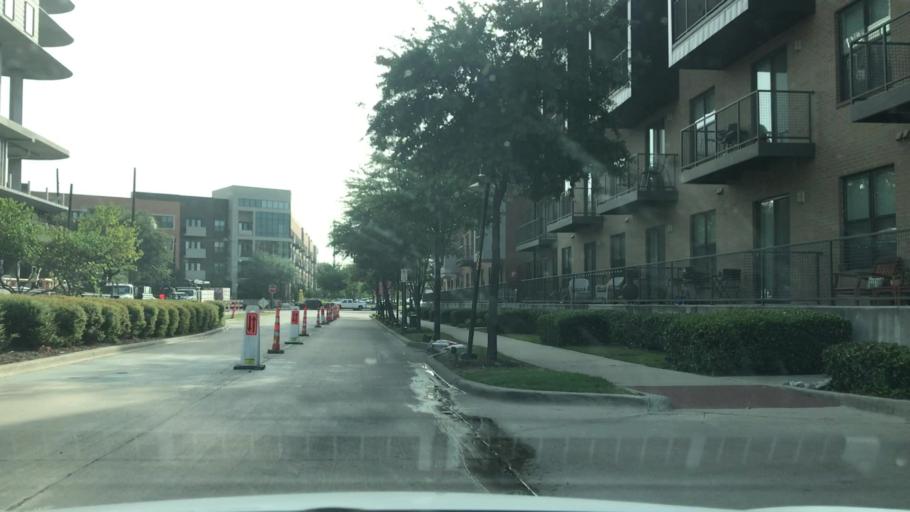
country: US
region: Texas
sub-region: Dallas County
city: Dallas
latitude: 32.7963
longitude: -96.8223
